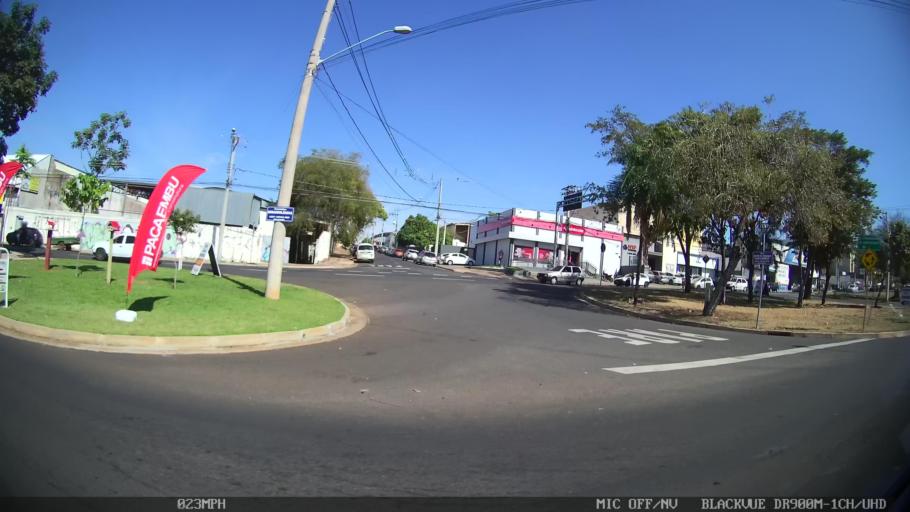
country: BR
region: Sao Paulo
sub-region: Sao Jose Do Rio Preto
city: Sao Jose do Rio Preto
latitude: -20.7799
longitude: -49.4013
